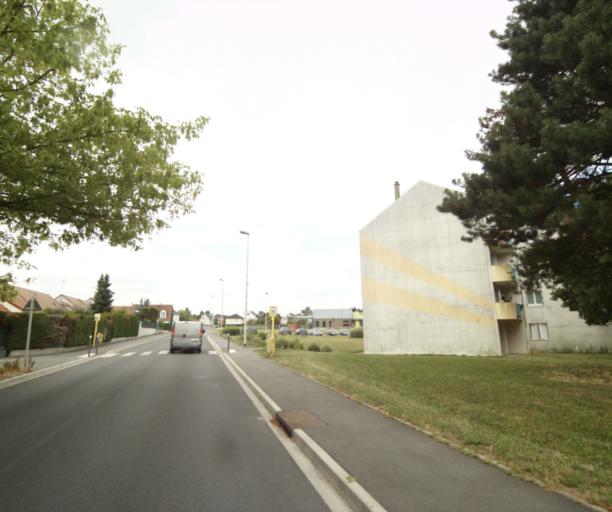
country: FR
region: Centre
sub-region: Departement du Loiret
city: Saran
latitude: 47.9385
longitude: 1.8741
